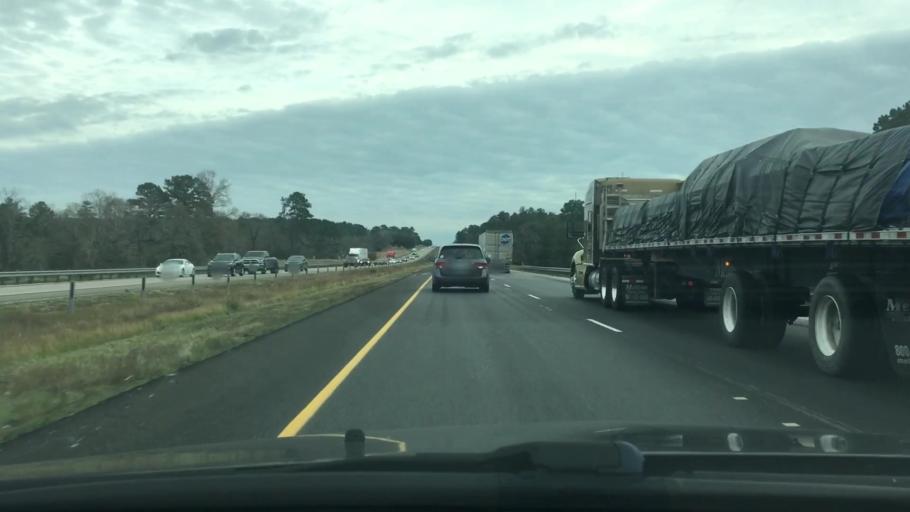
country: US
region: Texas
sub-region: Walker County
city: Huntsville
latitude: 30.8258
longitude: -95.7078
